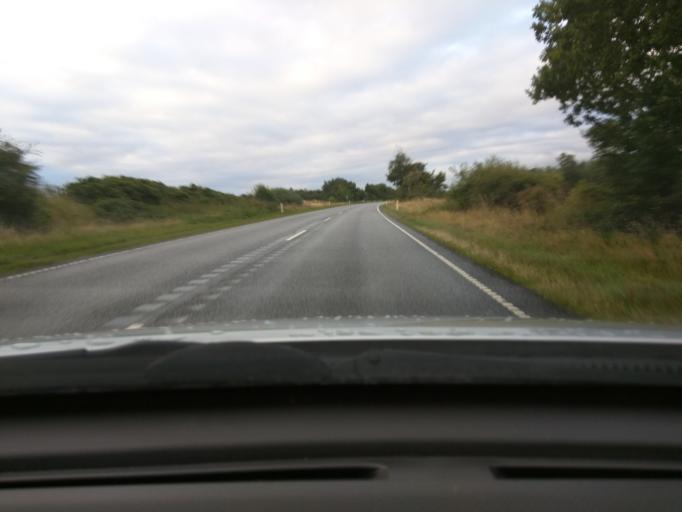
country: DK
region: Central Jutland
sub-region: Viborg Kommune
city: Viborg
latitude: 56.3773
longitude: 9.3792
